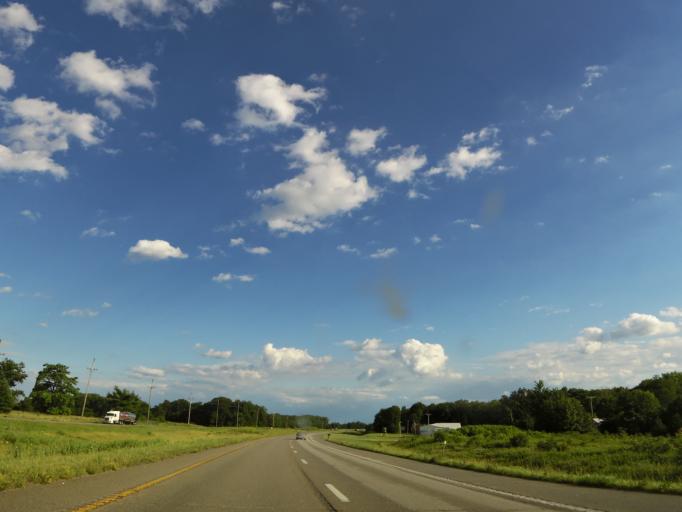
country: US
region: Missouri
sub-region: Lincoln County
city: Troy
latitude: 39.1173
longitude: -90.9606
